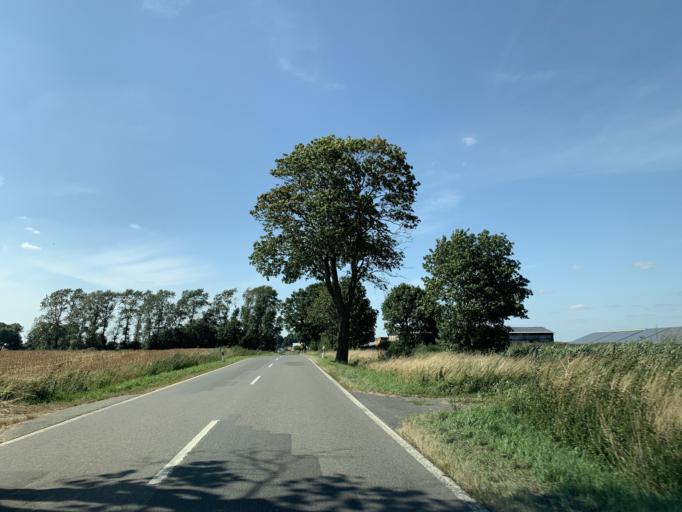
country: DE
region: Mecklenburg-Vorpommern
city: Blankensee
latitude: 53.3900
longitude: 13.3227
